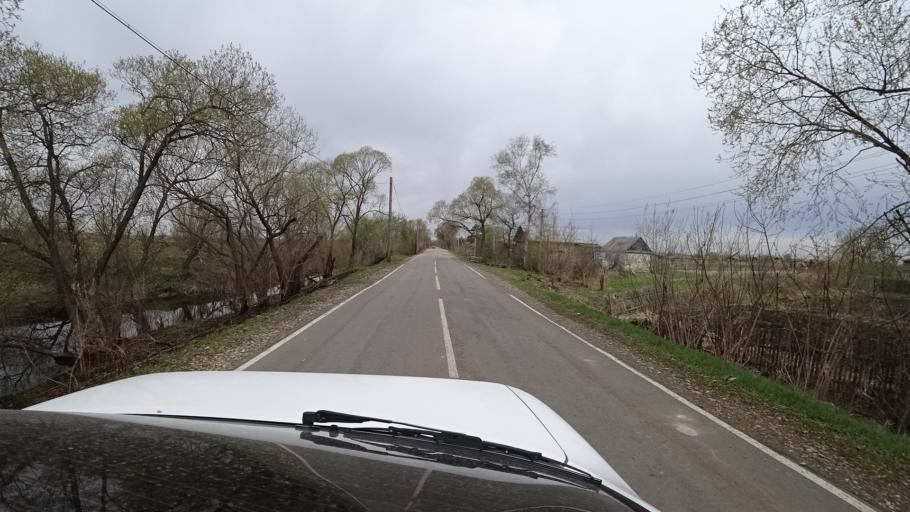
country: RU
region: Primorskiy
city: Dal'nerechensk
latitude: 45.9715
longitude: 133.7568
